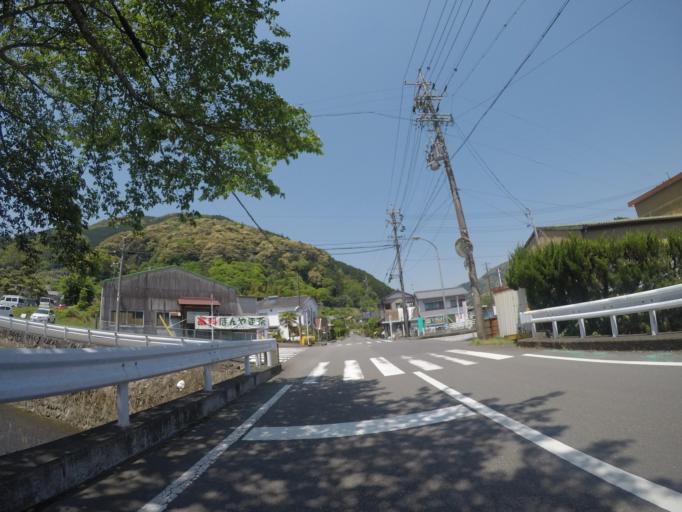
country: JP
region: Shizuoka
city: Shizuoka-shi
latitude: 35.0058
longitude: 138.2757
